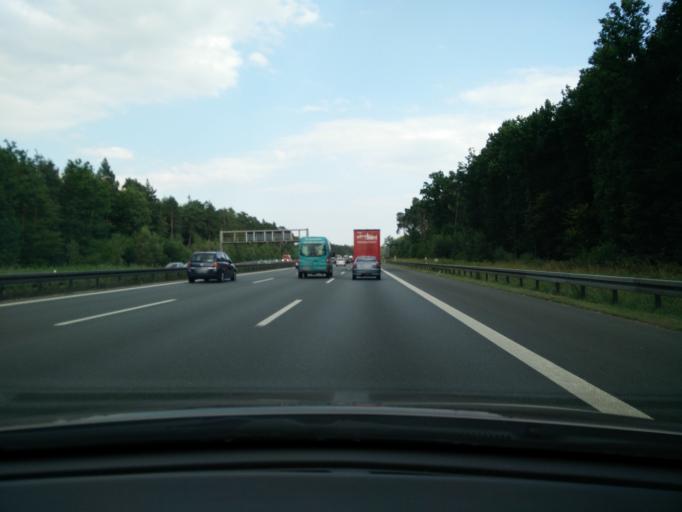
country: DE
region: Bavaria
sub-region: Regierungsbezirk Mittelfranken
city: Buckenhof
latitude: 49.5320
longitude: 11.0520
